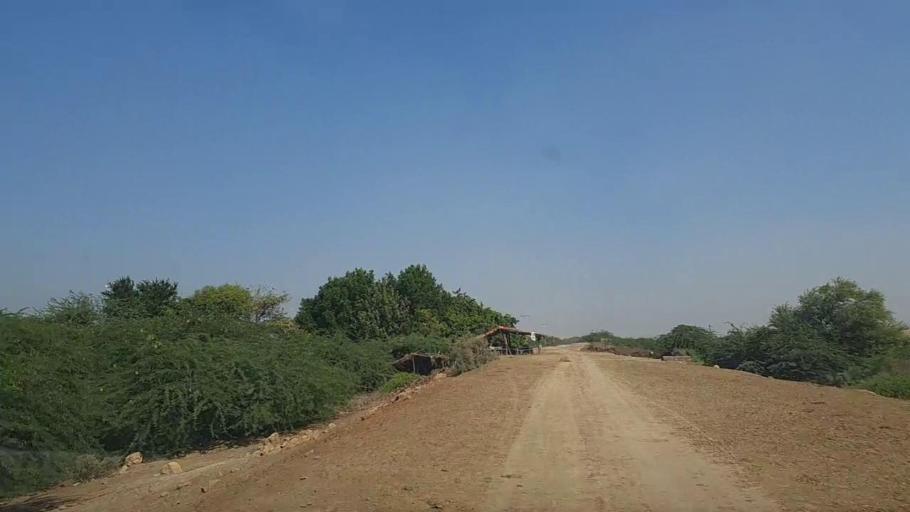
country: PK
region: Sindh
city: Daro Mehar
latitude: 24.8881
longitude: 68.0613
